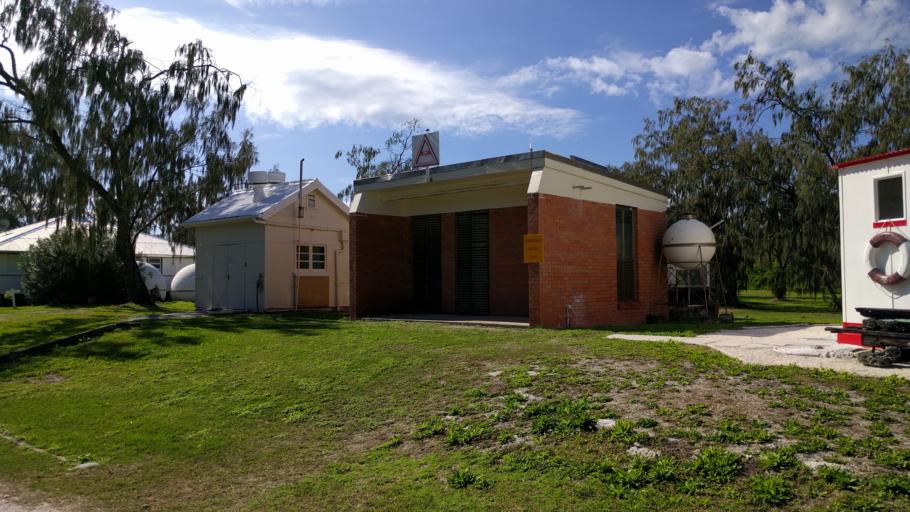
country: AU
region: Queensland
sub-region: Bundaberg
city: Bundaberg
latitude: -24.1145
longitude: 152.7114
